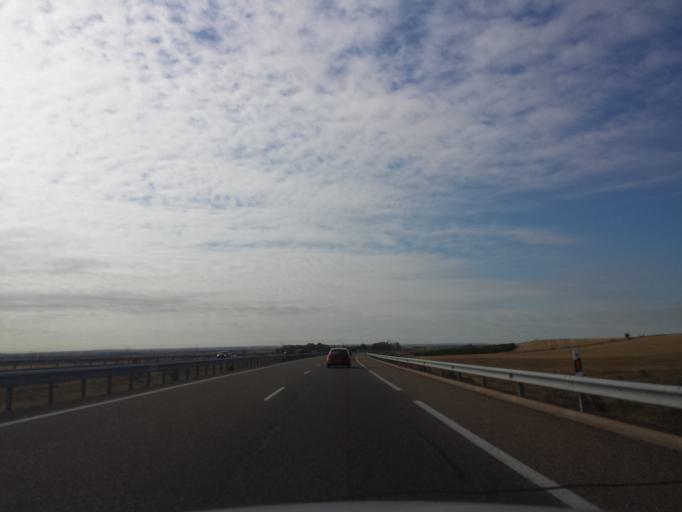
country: ES
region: Castille and Leon
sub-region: Provincia de Leon
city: Ardon
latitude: 42.4685
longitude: -5.5857
